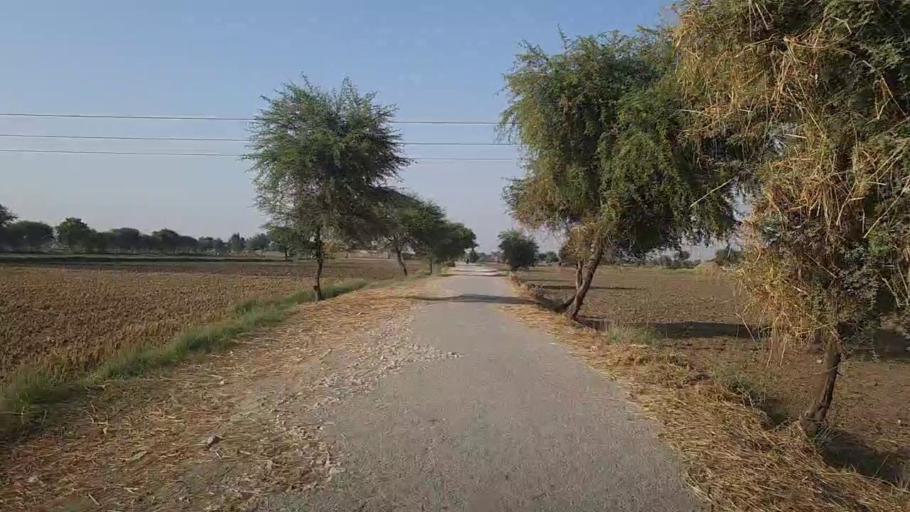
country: PK
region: Sindh
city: Kashmor
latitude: 28.4106
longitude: 69.4121
